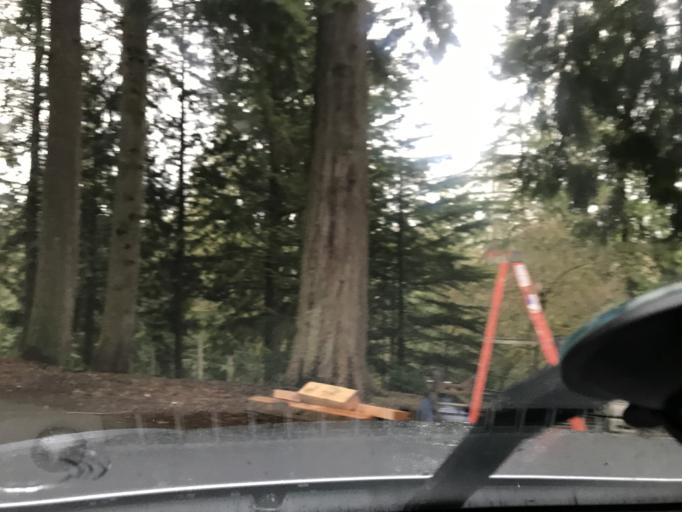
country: US
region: Washington
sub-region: King County
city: Ames Lake
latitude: 47.6506
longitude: -121.9569
